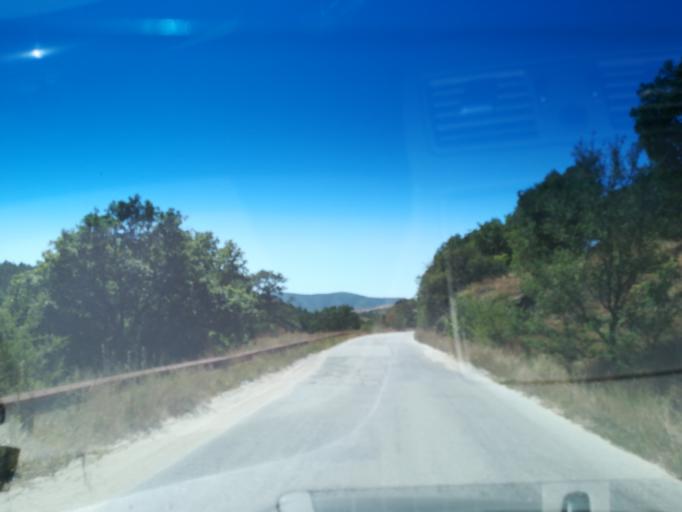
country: BG
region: Pazardzhik
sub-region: Obshtina Strelcha
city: Strelcha
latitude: 42.5253
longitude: 24.3257
